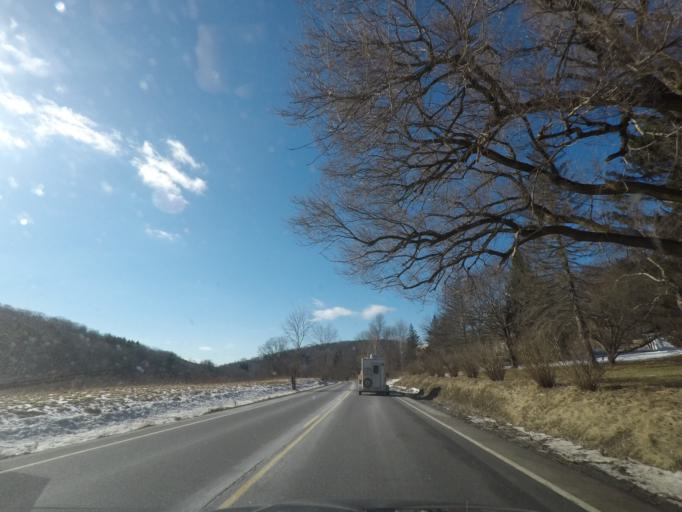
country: US
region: Massachusetts
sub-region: Berkshire County
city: Richmond
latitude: 42.4189
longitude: -73.4655
